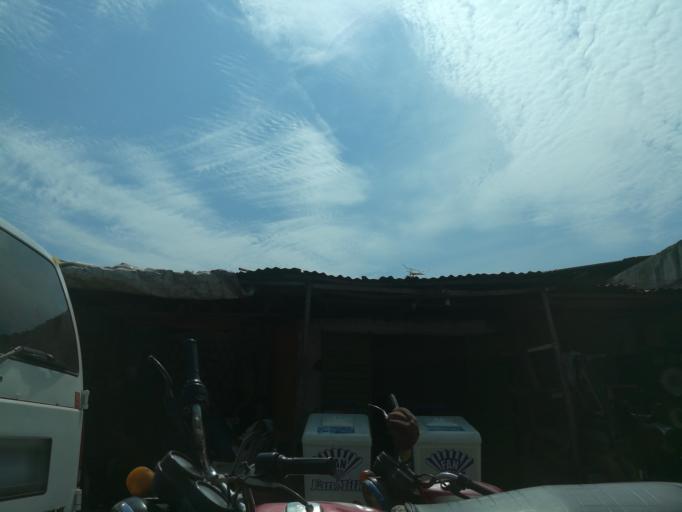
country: NG
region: Lagos
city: Ikorodu
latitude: 6.6286
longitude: 3.4827
